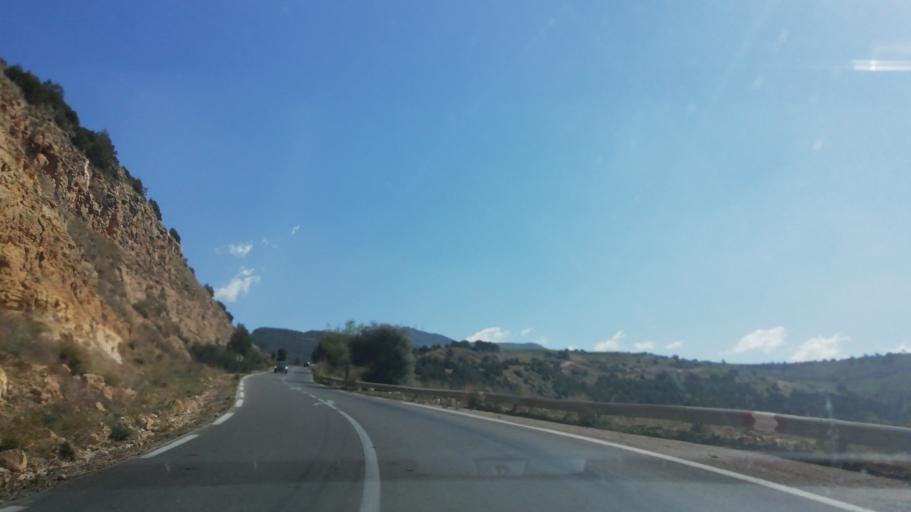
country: DZ
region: Mascara
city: Mascara
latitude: 35.4989
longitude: 0.1305
